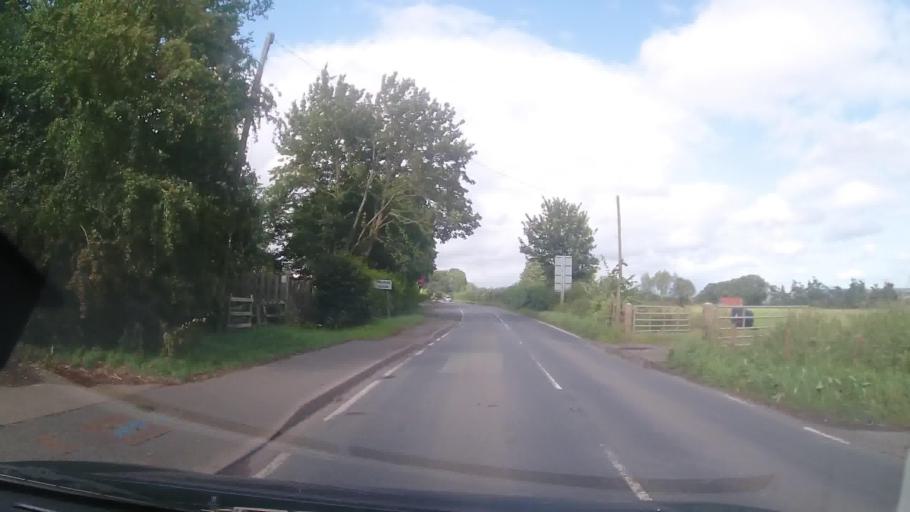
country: GB
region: England
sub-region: Shropshire
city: Bishop's Castle
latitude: 52.4899
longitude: -2.9927
